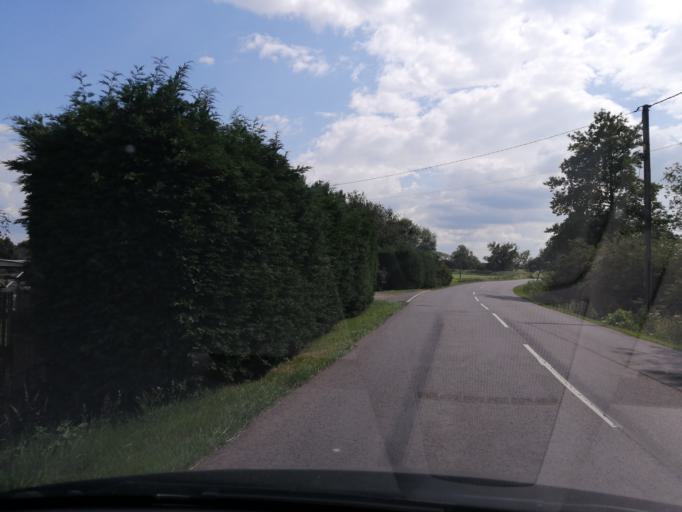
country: GB
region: England
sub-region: Cambridgeshire
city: Ramsey
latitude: 52.4484
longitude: -0.1589
